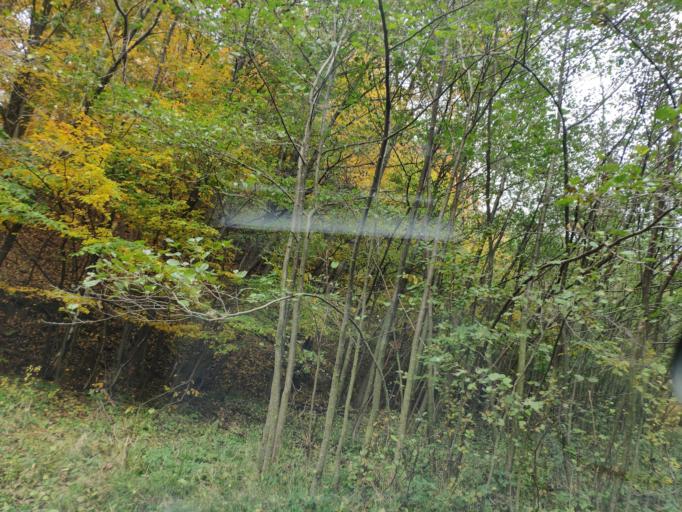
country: SK
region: Kosicky
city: Medzev
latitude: 48.7264
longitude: 20.9864
